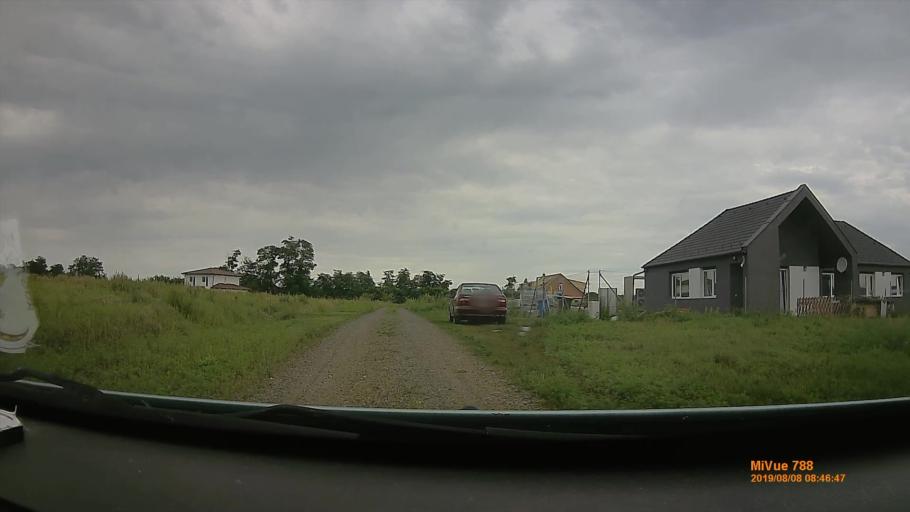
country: HU
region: Hajdu-Bihar
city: Debrecen
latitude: 47.5979
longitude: 21.6375
